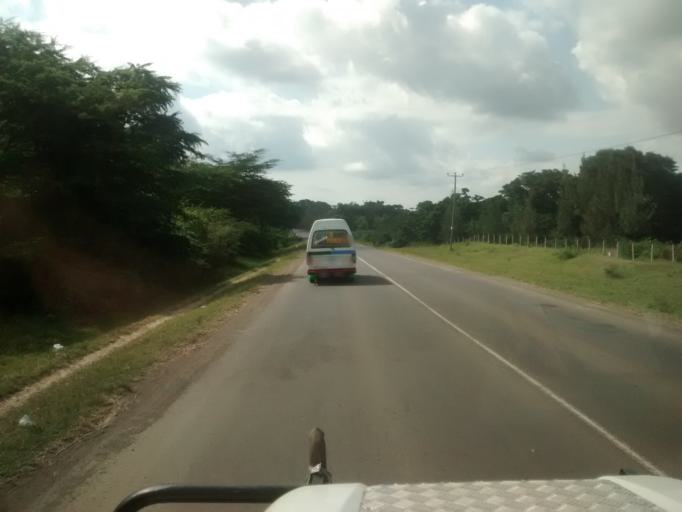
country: TZ
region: Arusha
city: Usa River
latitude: -3.3748
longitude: 36.8291
